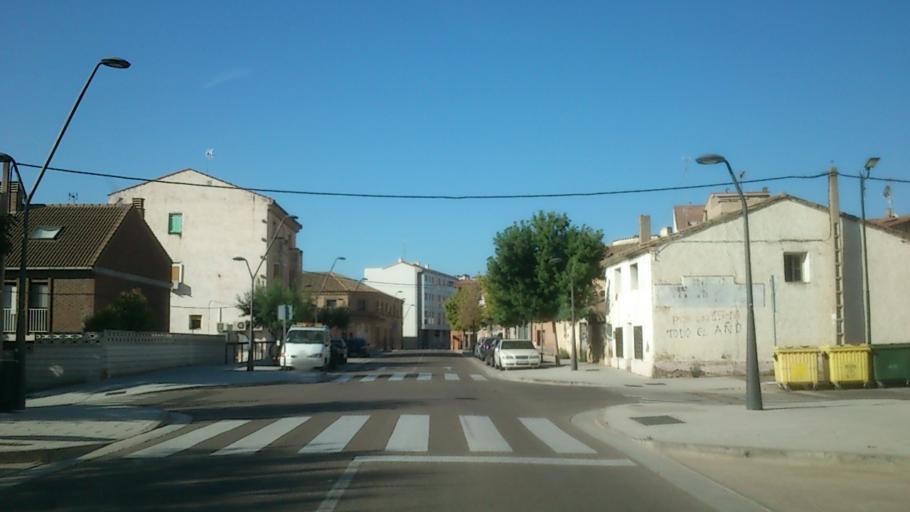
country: ES
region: Aragon
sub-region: Provincia de Zaragoza
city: Villanueva de Gallego
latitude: 41.7701
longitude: -0.8224
